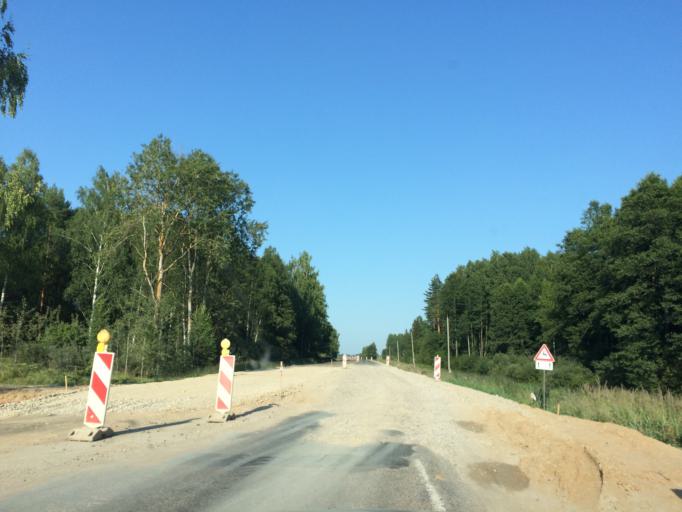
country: LV
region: Rezekne
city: Rezekne
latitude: 56.5145
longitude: 27.4872
